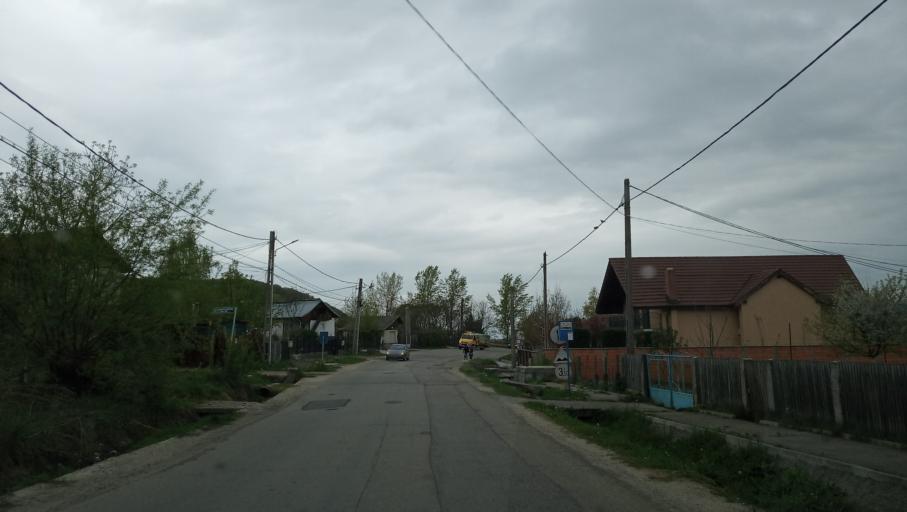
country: RO
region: Valcea
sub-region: Municipiul Ramnicu Valcea
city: Goranu
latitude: 45.1122
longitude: 24.3958
